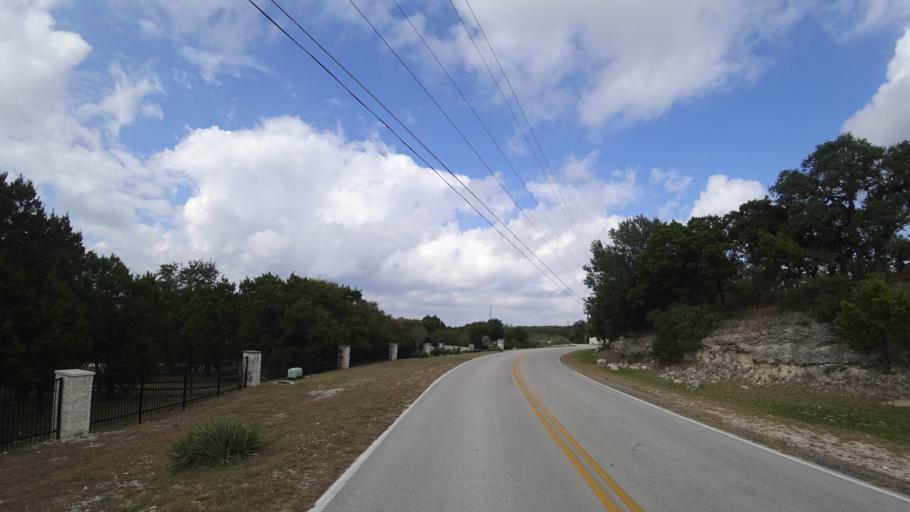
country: US
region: Texas
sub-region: Travis County
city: Barton Creek
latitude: 30.3035
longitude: -97.8779
